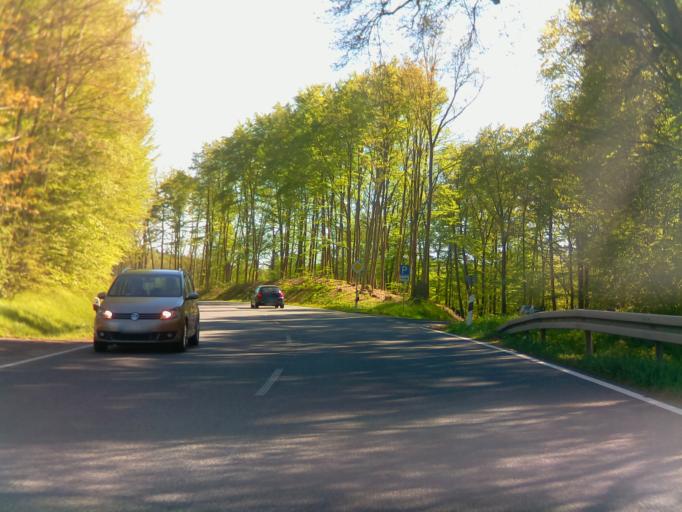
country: DE
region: Hesse
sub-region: Regierungsbezirk Giessen
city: Lauterbach
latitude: 50.6065
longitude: 9.3917
